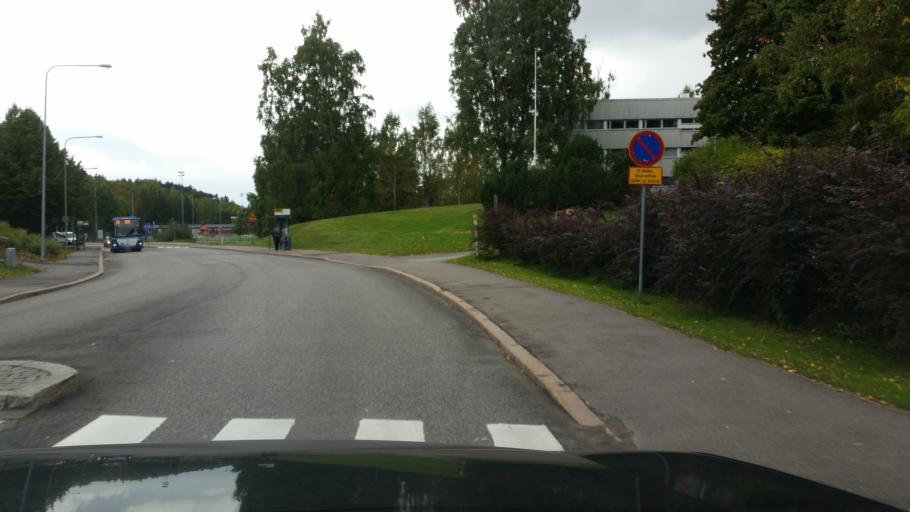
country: FI
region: Uusimaa
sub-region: Helsinki
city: Vantaa
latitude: 60.2405
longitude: 25.0033
